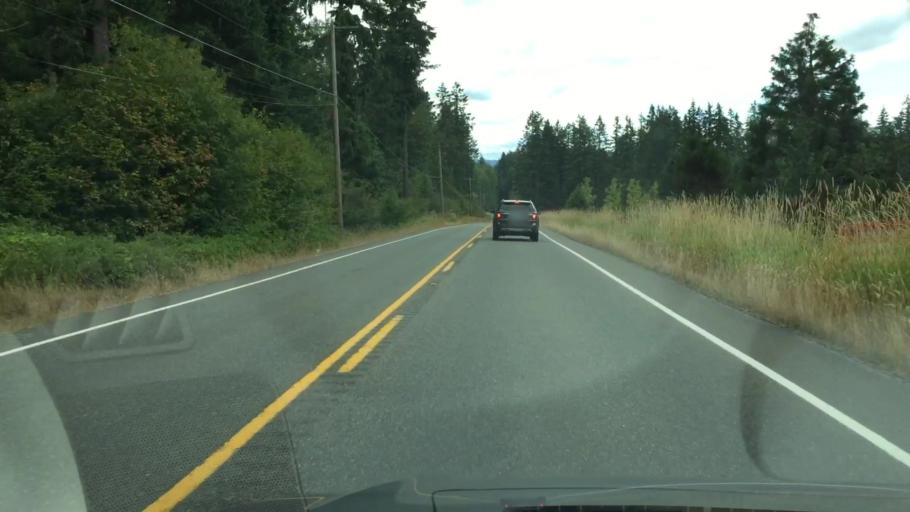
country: US
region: Washington
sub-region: Pierce County
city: Graham
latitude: 46.9577
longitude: -122.2974
